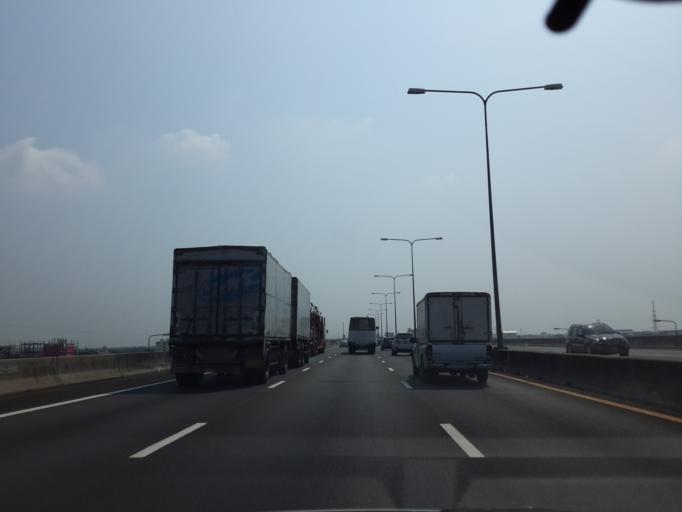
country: TH
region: Samut Prakan
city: Bang Sao Thong
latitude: 13.5906
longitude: 100.8248
